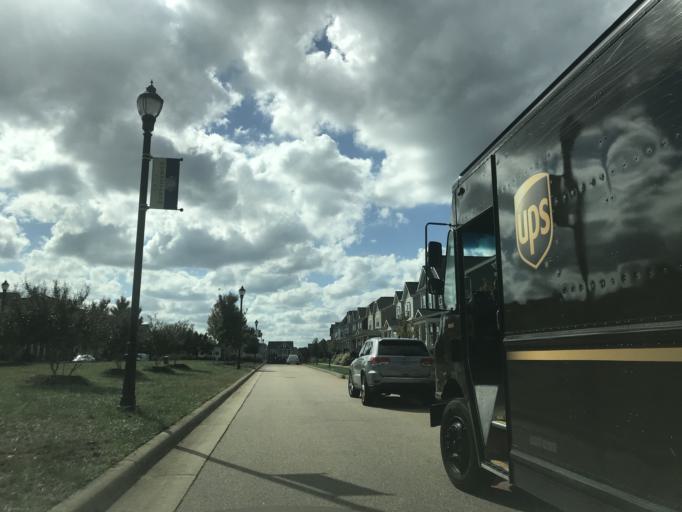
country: US
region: North Carolina
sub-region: Wake County
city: Raleigh
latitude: 35.7381
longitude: -78.6577
